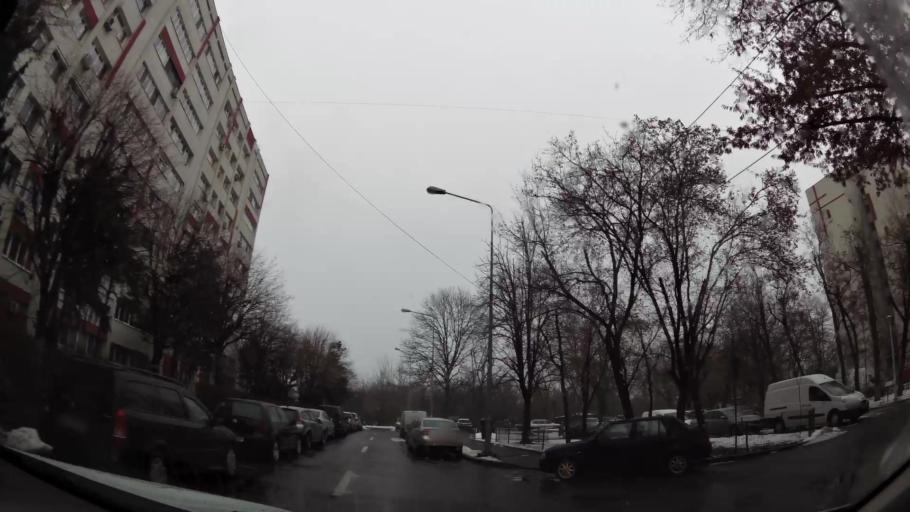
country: RO
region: Ilfov
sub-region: Comuna Chiajna
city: Rosu
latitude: 44.4810
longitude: 26.0535
